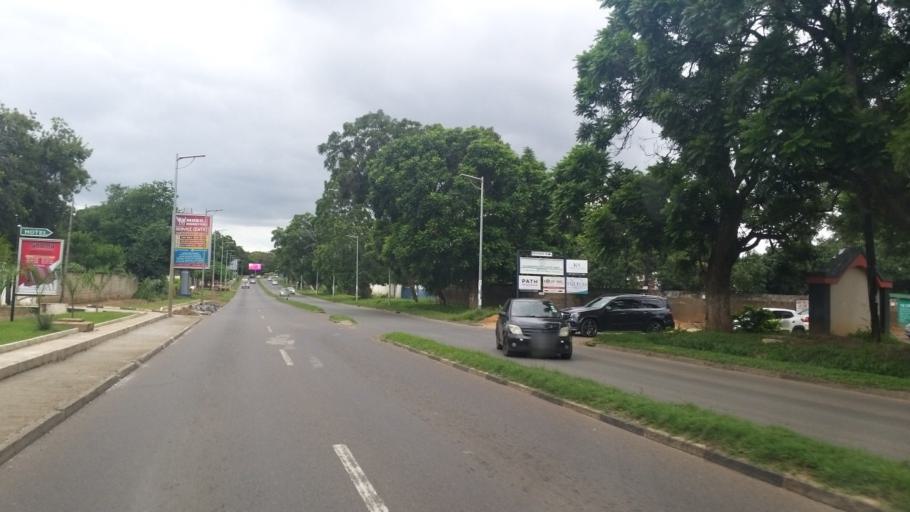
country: ZM
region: Lusaka
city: Lusaka
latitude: -15.4203
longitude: 28.3183
